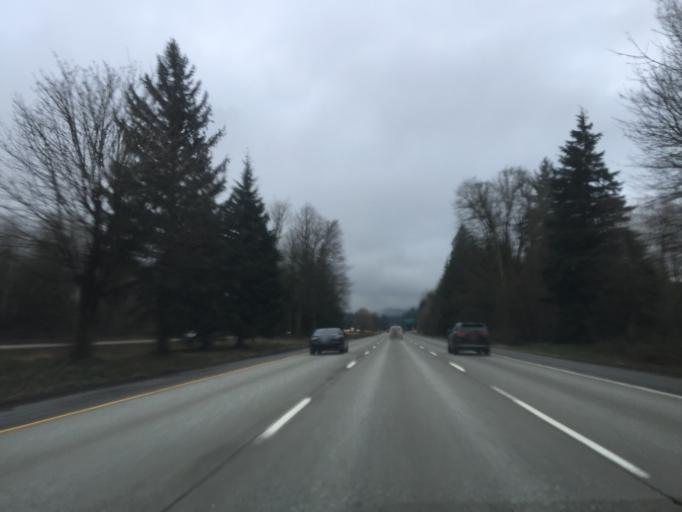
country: US
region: Washington
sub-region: King County
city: Riverbend
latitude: 47.4732
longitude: -121.7701
